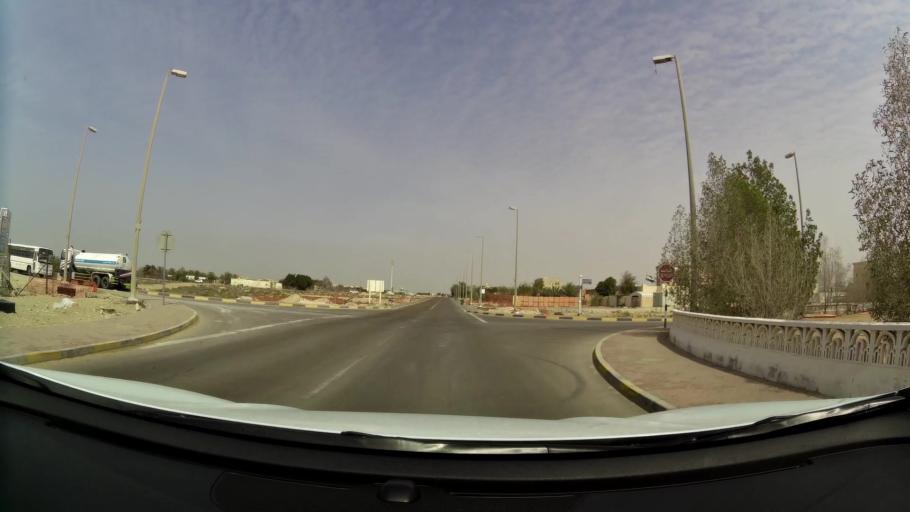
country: AE
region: Abu Dhabi
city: Abu Dhabi
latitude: 24.5344
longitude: 54.6693
